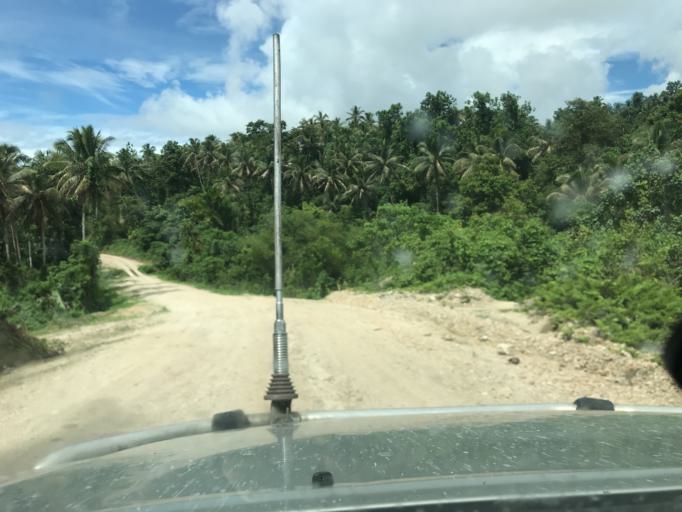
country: SB
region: Malaita
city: Auki
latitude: -8.4095
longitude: 160.7969
